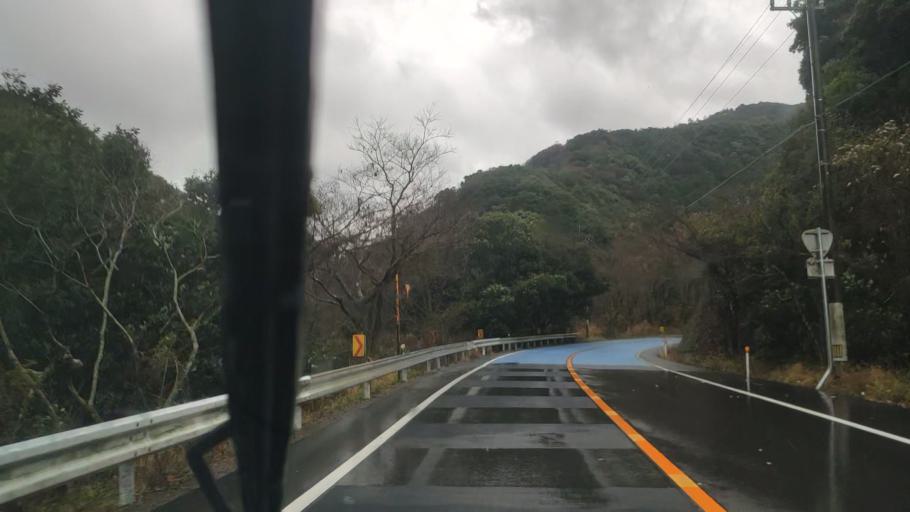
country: JP
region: Tokushima
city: Kamojimacho-jogejima
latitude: 34.1874
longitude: 134.3369
